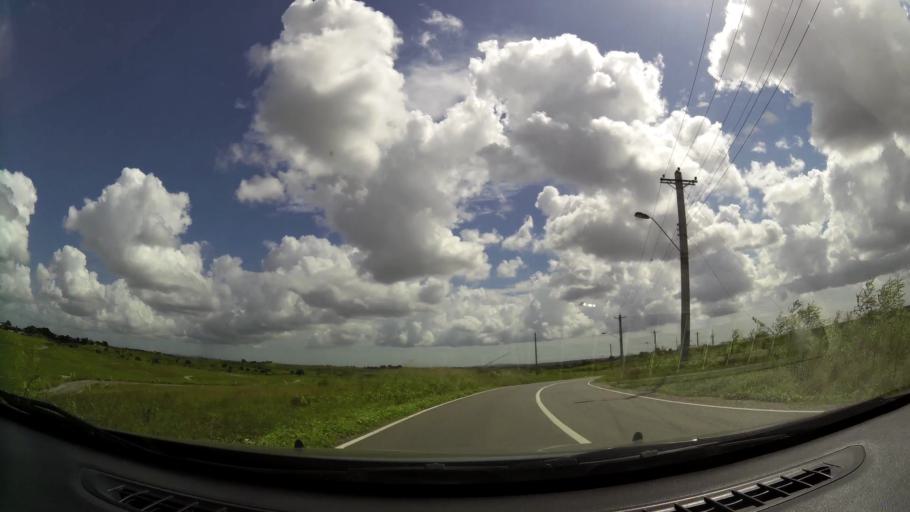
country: TT
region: City of San Fernando
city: San Fernando
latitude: 10.2389
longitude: -61.4976
